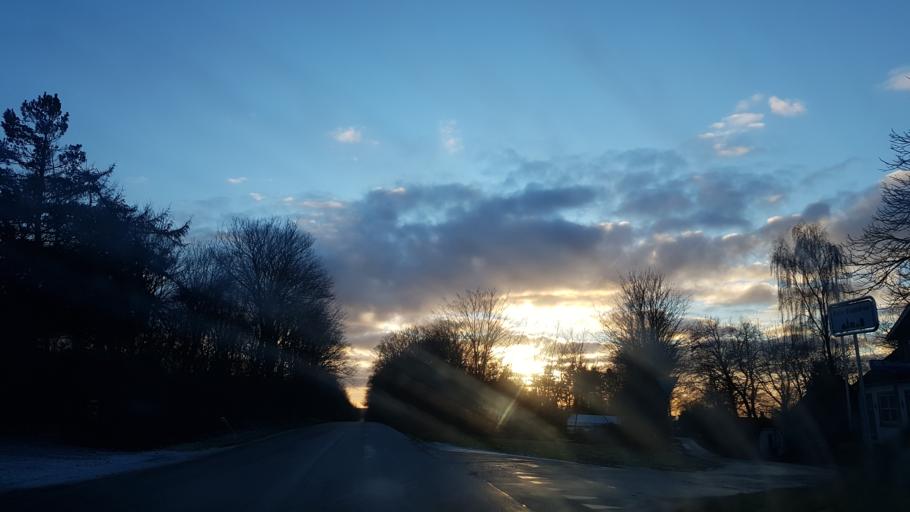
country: DK
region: South Denmark
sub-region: Kolding Kommune
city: Vamdrup
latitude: 55.3944
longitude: 9.3662
